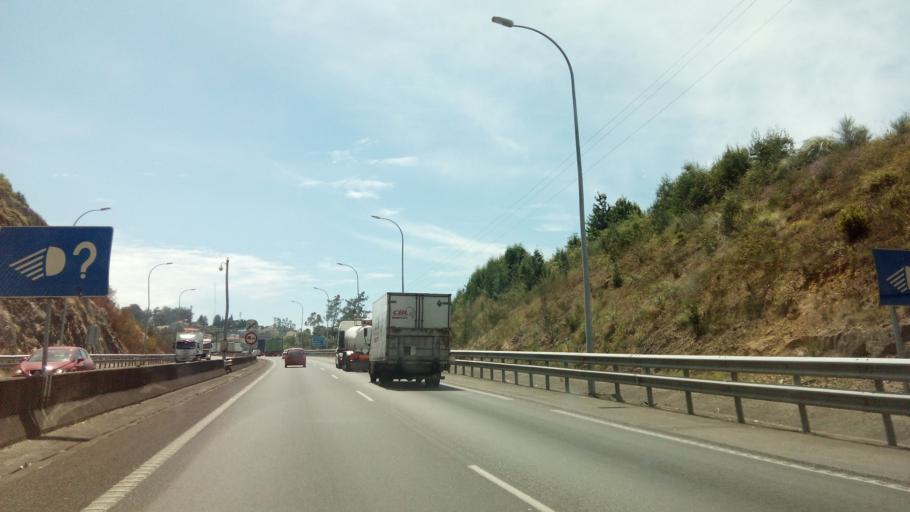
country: ES
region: Galicia
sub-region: Provincia de Pontevedra
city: Vigo
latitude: 42.2518
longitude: -8.6794
